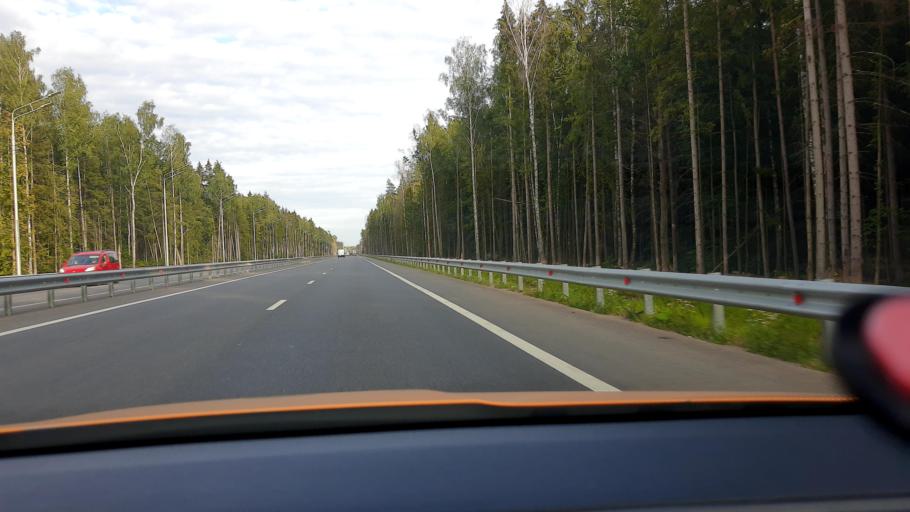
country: RU
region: Moskovskaya
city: Zvenigorod
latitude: 55.6721
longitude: 36.9124
